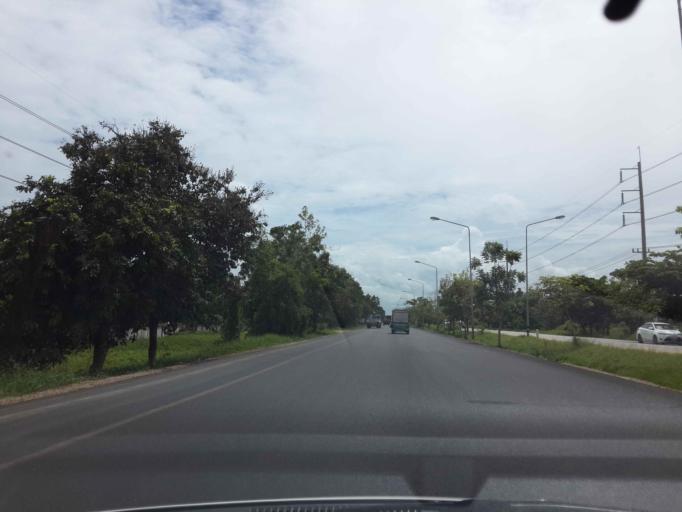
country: TH
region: Ratchaburi
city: Pak Tho
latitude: 13.4351
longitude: 99.8053
